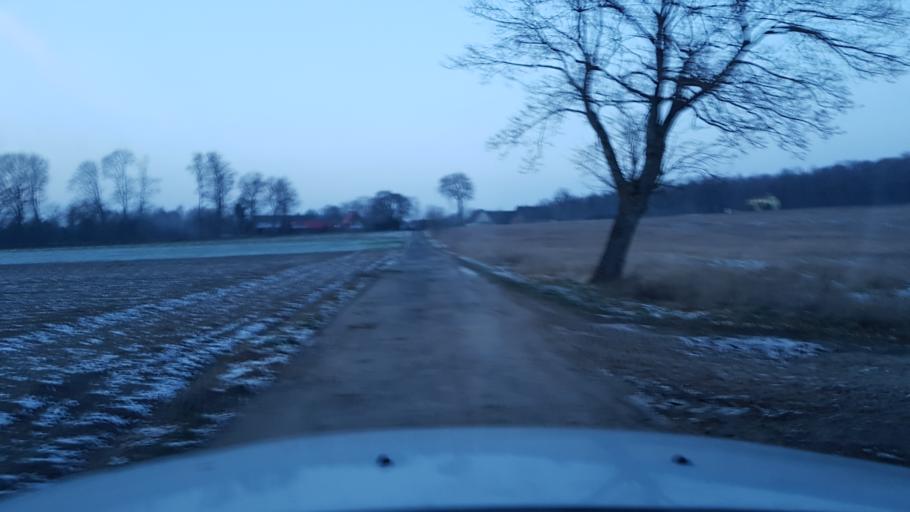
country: PL
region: West Pomeranian Voivodeship
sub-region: Powiat swidwinski
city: Slawoborze
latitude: 53.9673
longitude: 15.7649
